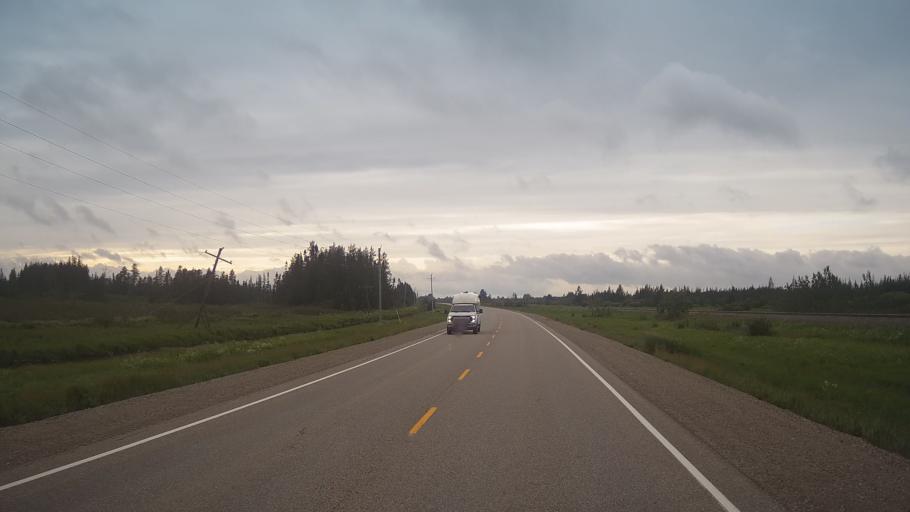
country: CA
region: Ontario
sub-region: Thunder Bay District
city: Thunder Bay
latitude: 48.8728
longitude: -89.9783
